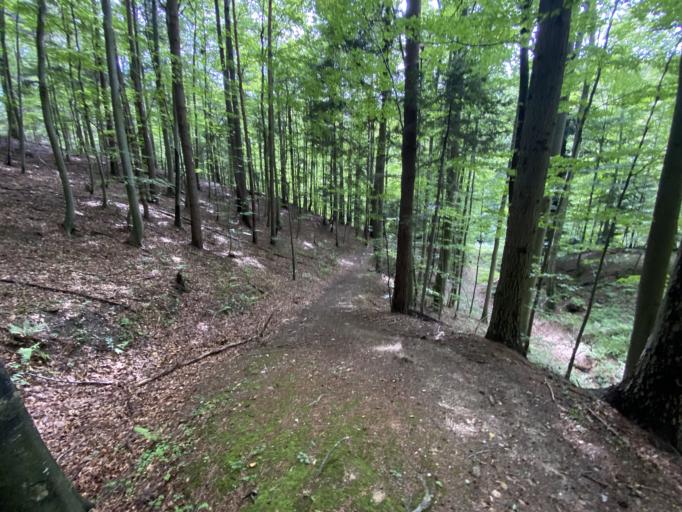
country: AT
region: Burgenland
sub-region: Politischer Bezirk Oberpullendorf
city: Kobersdorf
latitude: 47.5673
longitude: 16.3492
